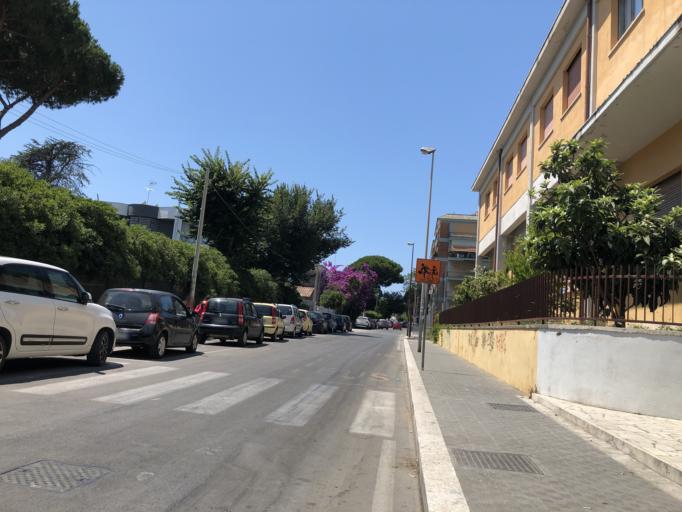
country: IT
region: Latium
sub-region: Citta metropolitana di Roma Capitale
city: Nettuno
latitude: 41.4579
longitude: 12.6529
